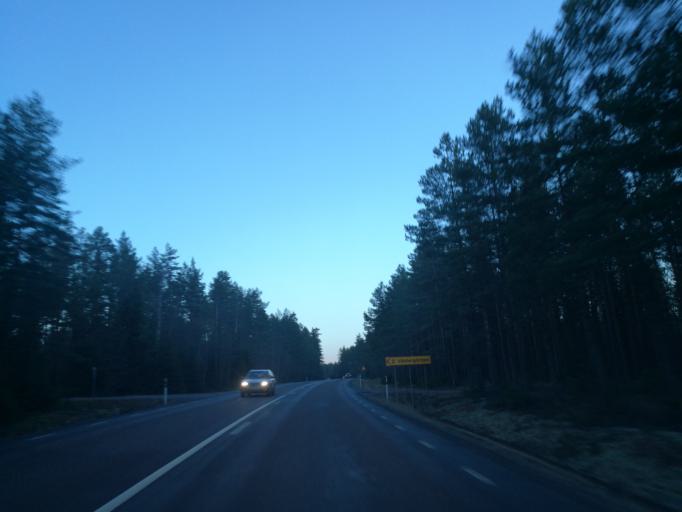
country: SE
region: Vaermland
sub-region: Eda Kommun
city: Charlottenberg
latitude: 59.8978
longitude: 12.2788
